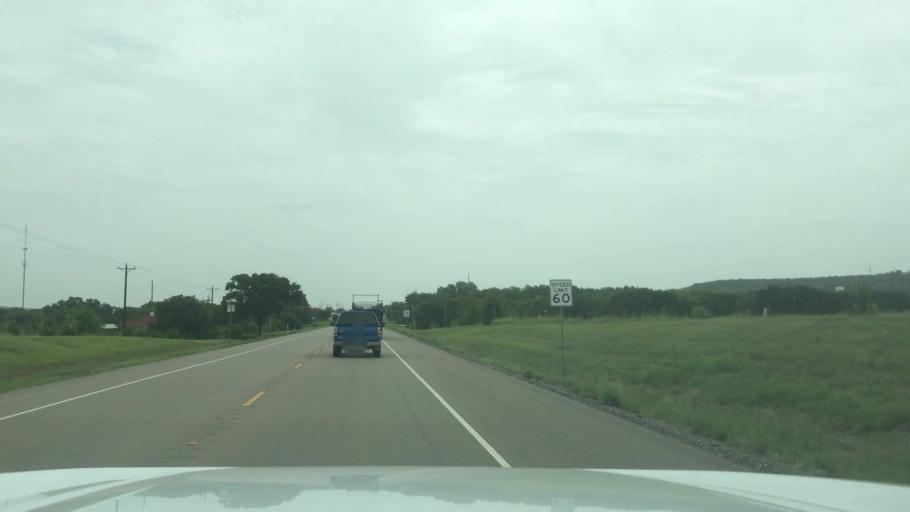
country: US
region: Texas
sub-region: Bosque County
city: Meridian
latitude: 31.9222
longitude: -97.6775
